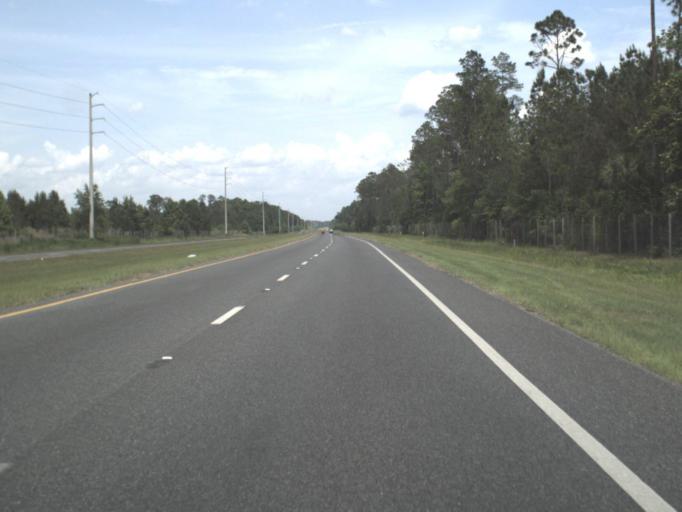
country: US
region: Florida
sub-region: Putnam County
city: Interlachen
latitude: 29.6271
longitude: -81.7805
